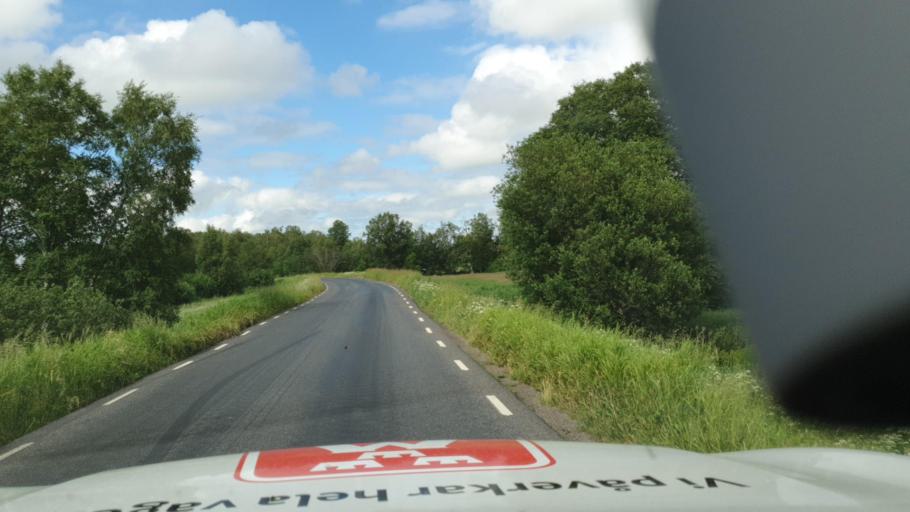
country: SE
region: Vaestra Goetaland
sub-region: Falkopings Kommun
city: Falkoeping
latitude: 58.0755
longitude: 13.6375
